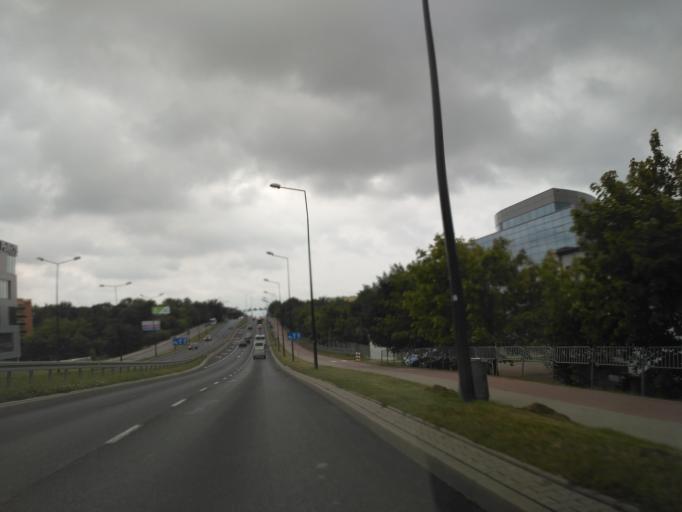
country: PL
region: Lublin Voivodeship
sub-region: Powiat lubelski
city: Lublin
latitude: 51.2737
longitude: 22.5735
